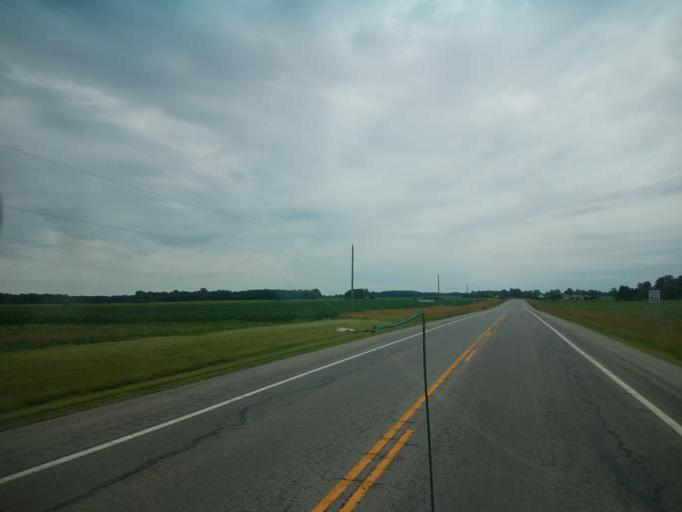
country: US
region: Ohio
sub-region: Hardin County
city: Ada
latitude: 40.7264
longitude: -83.7842
